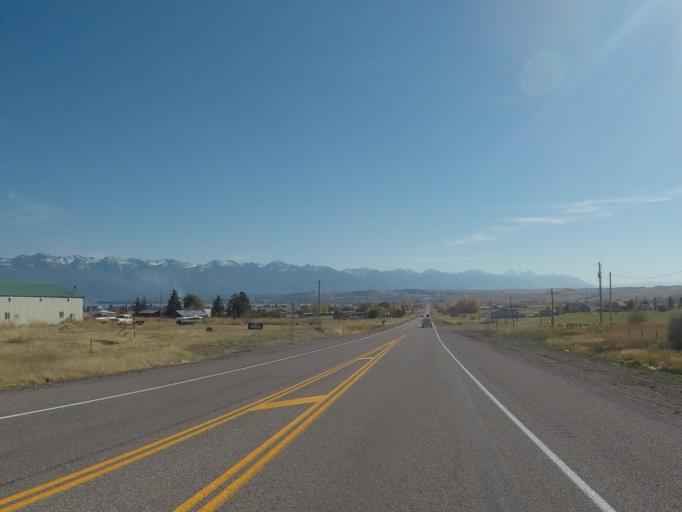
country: US
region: Montana
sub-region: Lake County
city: Polson
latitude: 47.7302
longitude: -114.2141
